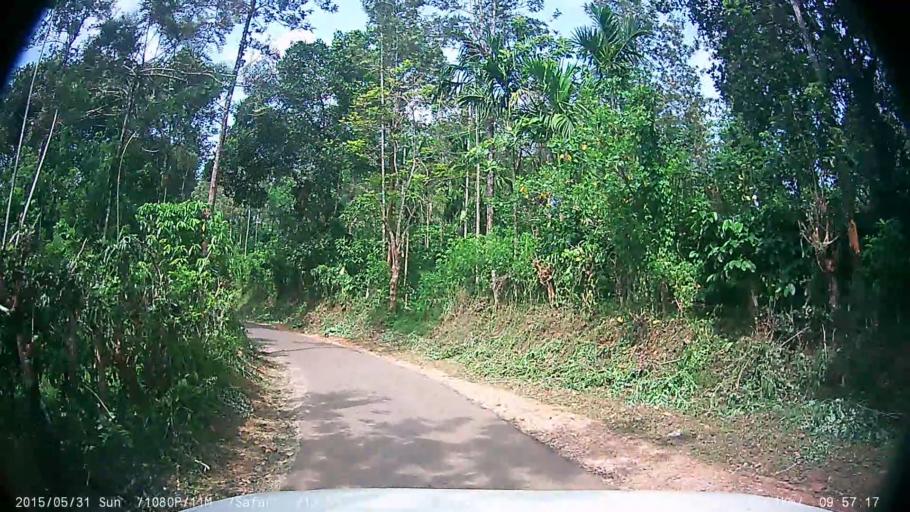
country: IN
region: Kerala
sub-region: Wayanad
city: Kalpetta
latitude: 11.5948
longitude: 76.0582
